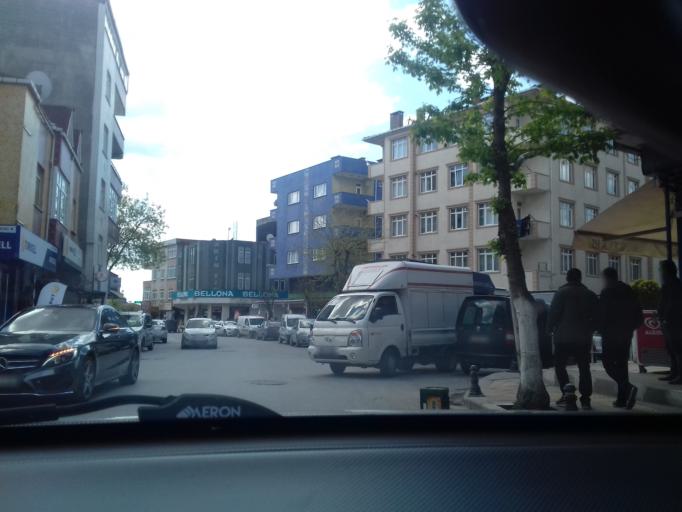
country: TR
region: Istanbul
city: Pendik
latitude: 40.8796
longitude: 29.2866
